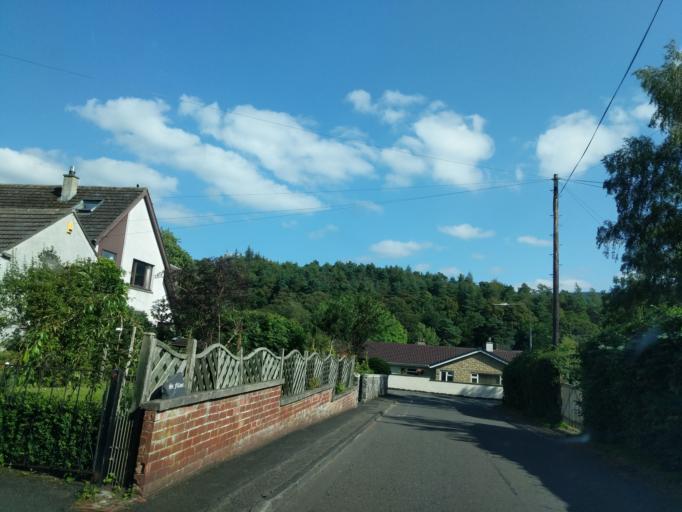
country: GB
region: Scotland
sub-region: The Scottish Borders
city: Innerleithen
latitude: 55.6230
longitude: -3.0639
